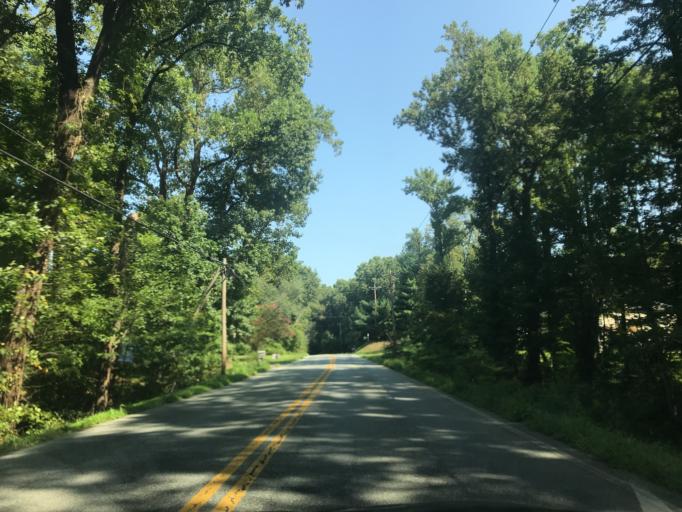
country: US
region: Maryland
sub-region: Calvert County
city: Prince Frederick
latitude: 38.5051
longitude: -76.6227
